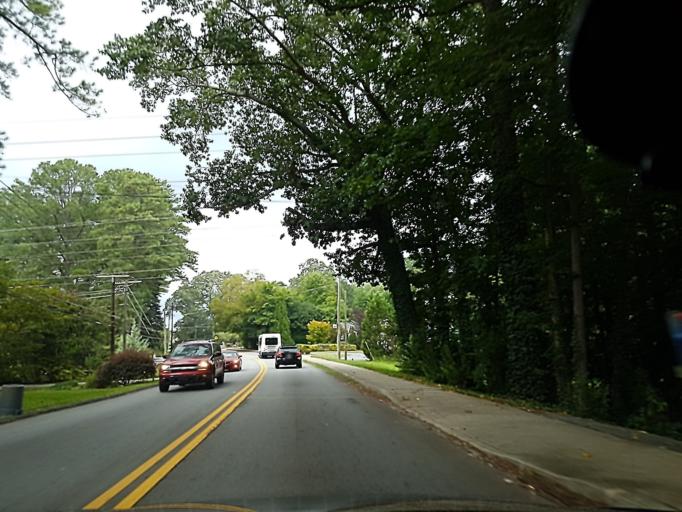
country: US
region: Georgia
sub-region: DeKalb County
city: North Druid Hills
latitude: 33.8168
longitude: -84.3456
